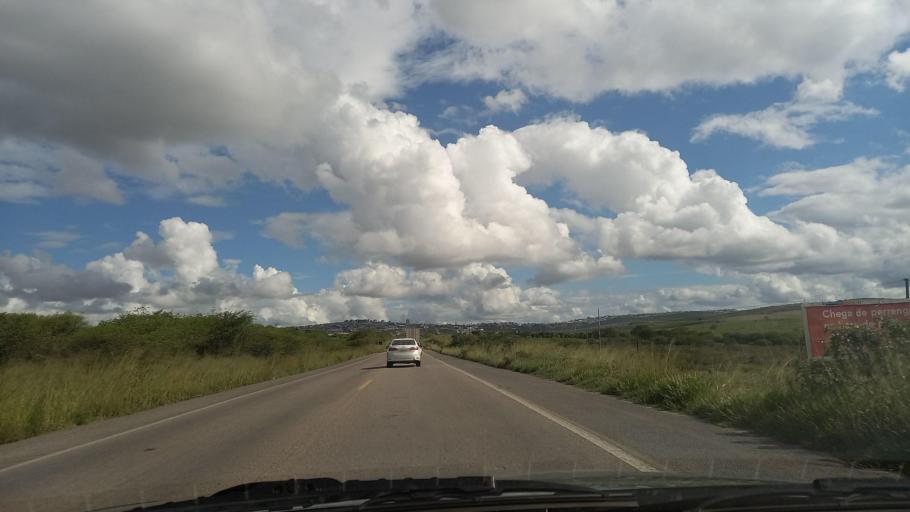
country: BR
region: Pernambuco
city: Garanhuns
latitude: -8.8375
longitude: -36.4561
